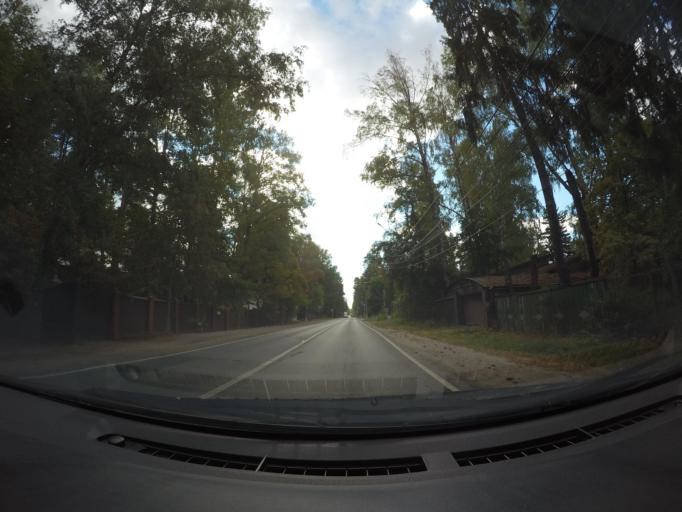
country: RU
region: Moskovskaya
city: Il'inskiy
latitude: 55.6269
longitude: 38.1093
